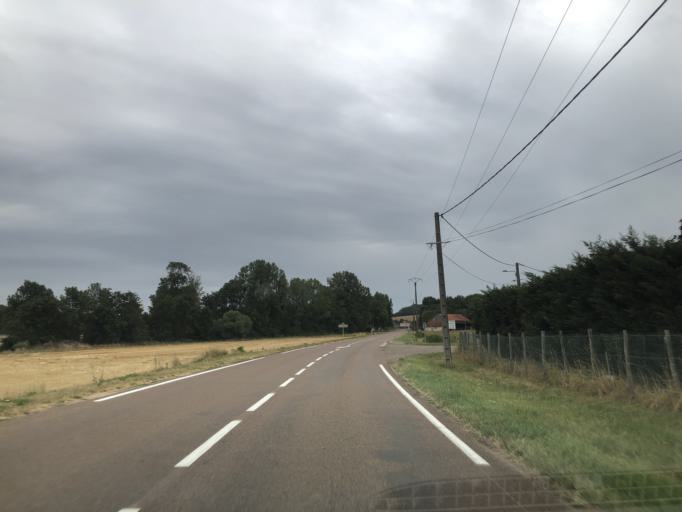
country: FR
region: Bourgogne
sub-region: Departement de l'Yonne
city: Saint-Julien-du-Sault
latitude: 47.9365
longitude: 3.2396
